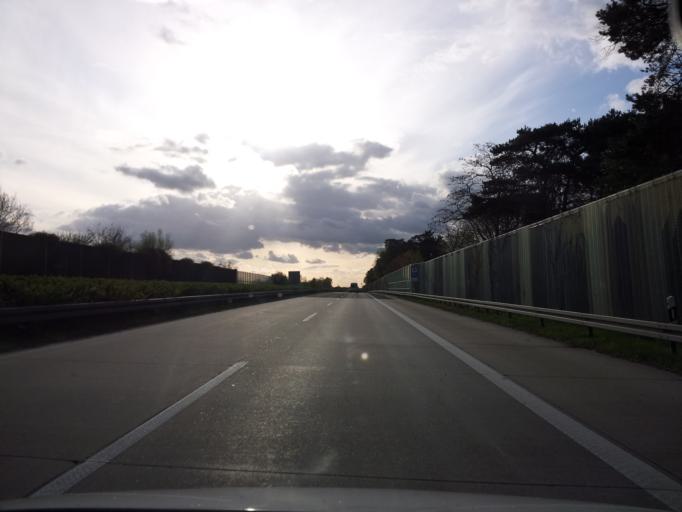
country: DE
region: Brandenburg
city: Cottbus
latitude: 51.7173
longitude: 14.3388
